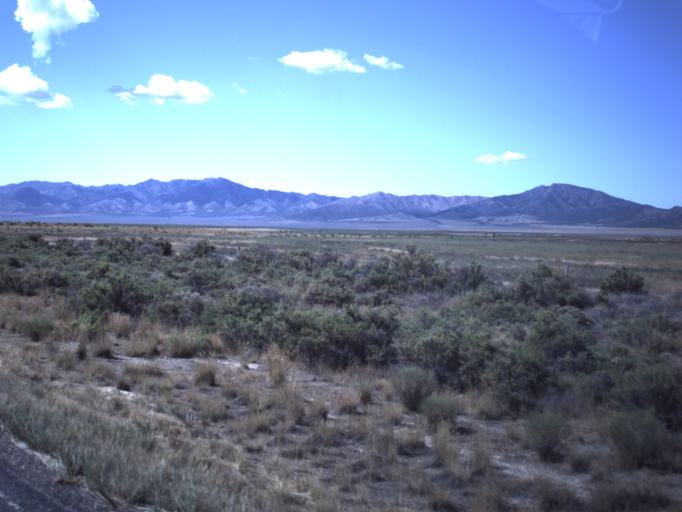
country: US
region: Utah
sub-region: Tooele County
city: Tooele
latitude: 40.1448
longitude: -112.4308
